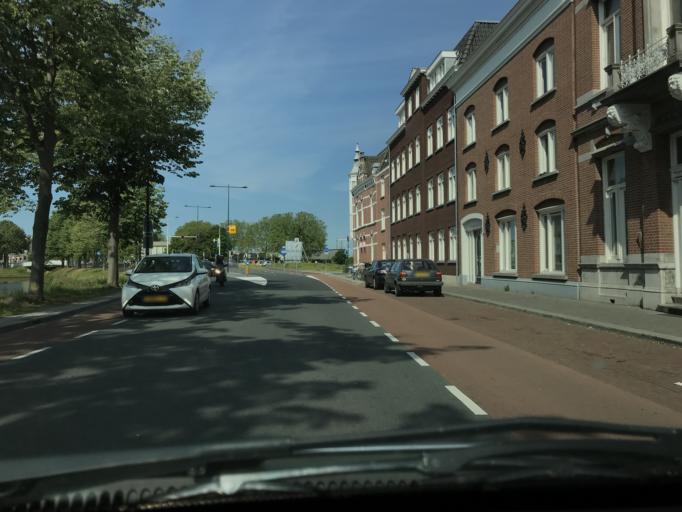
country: NL
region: North Brabant
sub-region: Gemeente Breda
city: Breda
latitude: 51.5934
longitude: 4.7742
